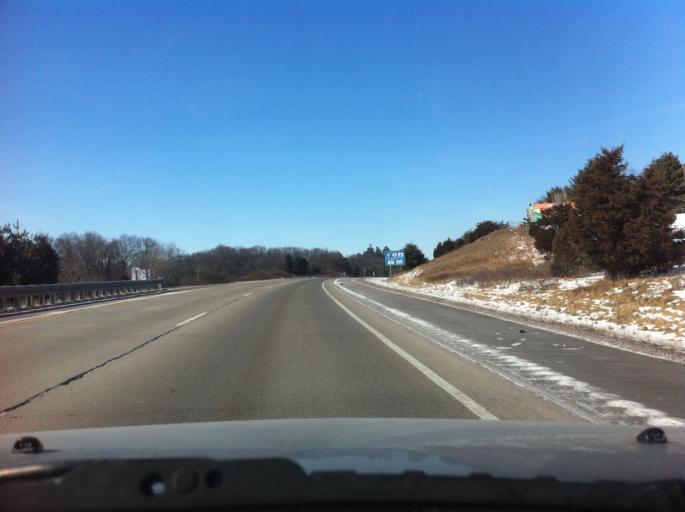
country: US
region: Wisconsin
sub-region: Sauk County
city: Lake Delton
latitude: 43.5644
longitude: -89.7391
